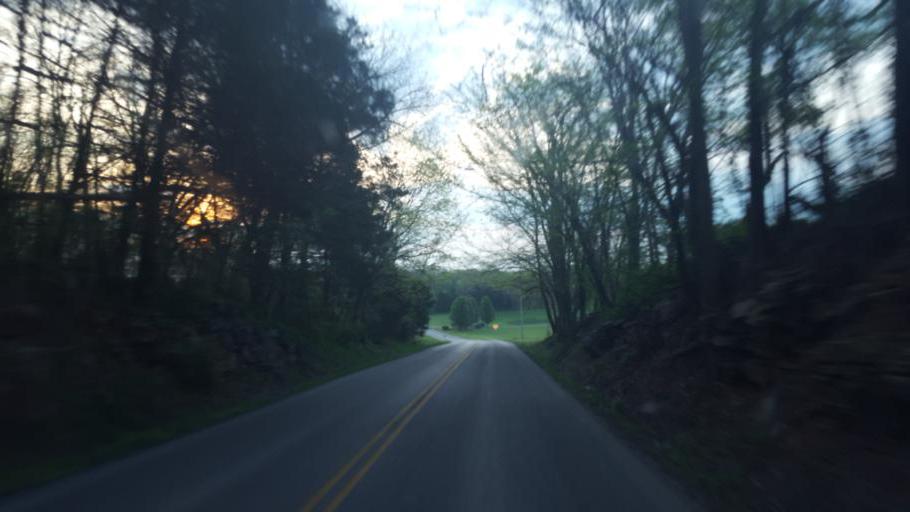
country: US
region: Kentucky
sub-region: Hart County
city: Munfordville
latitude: 37.2741
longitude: -85.9089
